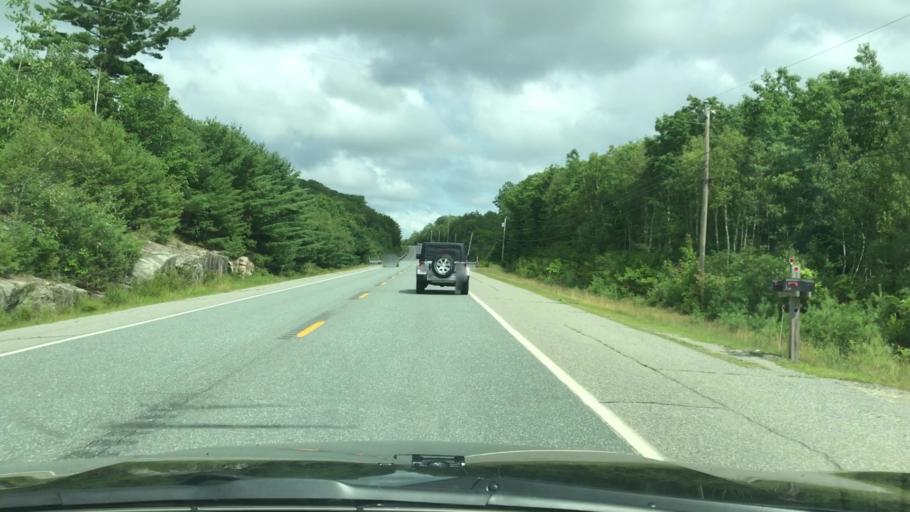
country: US
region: Maine
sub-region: Hancock County
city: Surry
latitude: 44.5654
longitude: -68.6077
